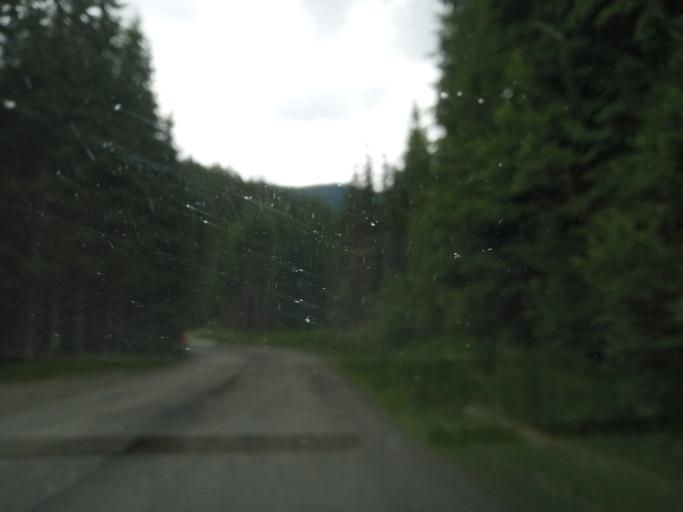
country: RO
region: Valcea
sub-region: Comuna Voineasa
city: Voineasa
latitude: 45.4139
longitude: 23.7248
